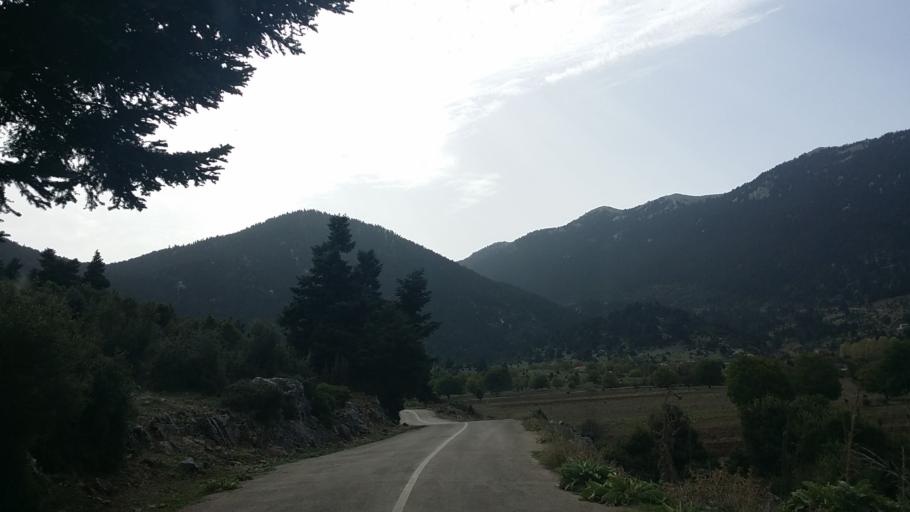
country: GR
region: Central Greece
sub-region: Nomos Voiotias
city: Livadeia
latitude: 38.3740
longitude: 22.8462
